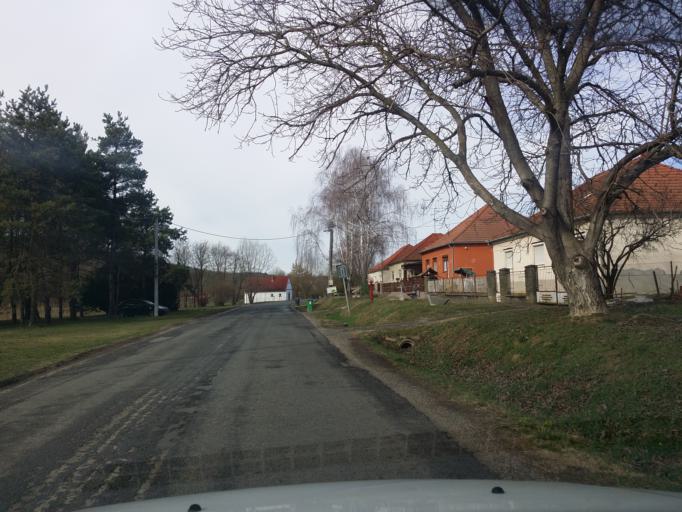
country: HU
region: Baranya
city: Villany
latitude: 45.8803
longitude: 18.4326
